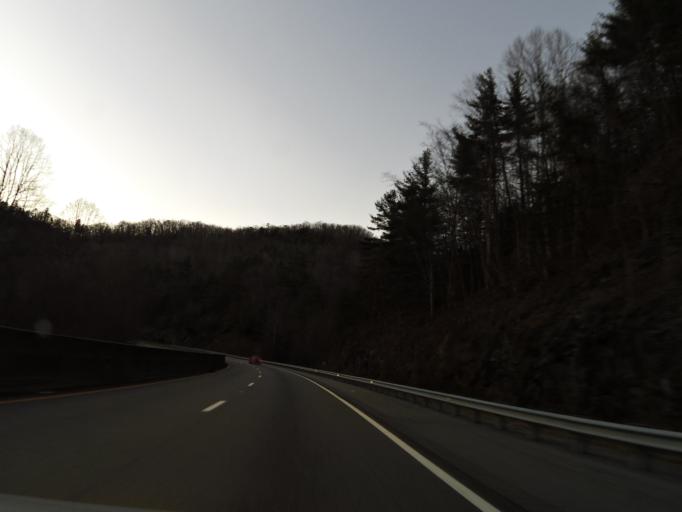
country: US
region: North Carolina
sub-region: Haywood County
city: Cove Creek
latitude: 35.7561
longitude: -83.0347
